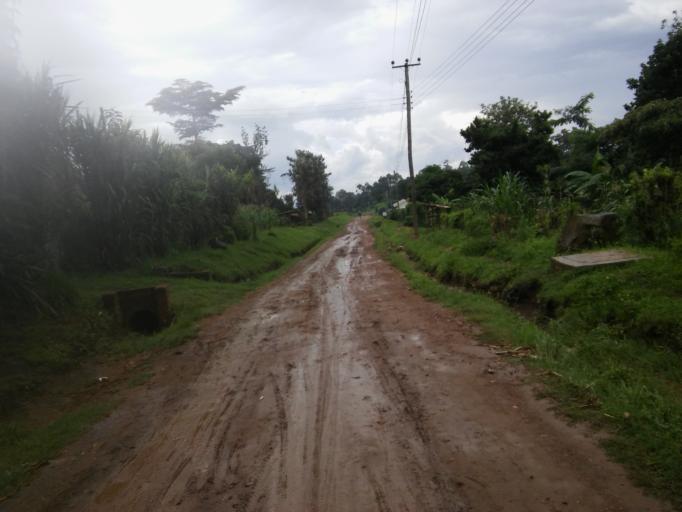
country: UG
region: Eastern Region
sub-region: Mbale District
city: Mbale
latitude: 1.0346
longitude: 34.1956
